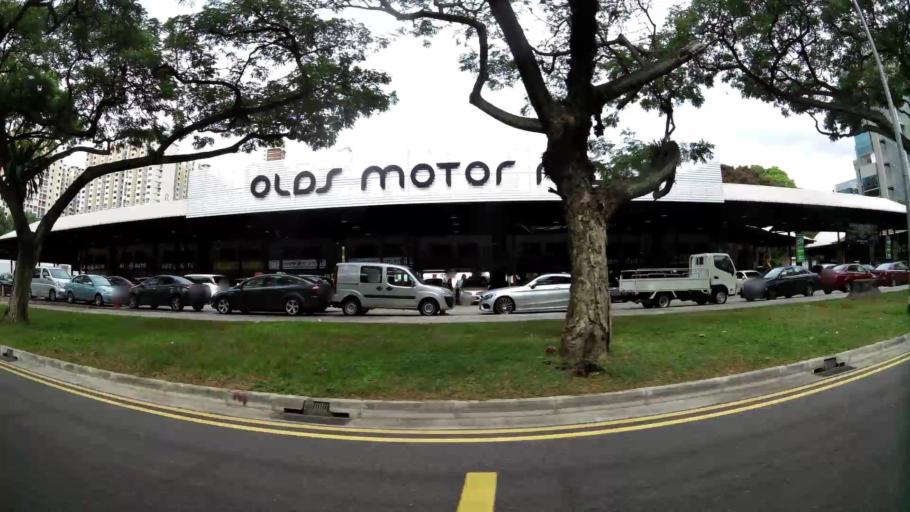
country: SG
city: Singapore
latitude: 1.3051
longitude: 103.7954
